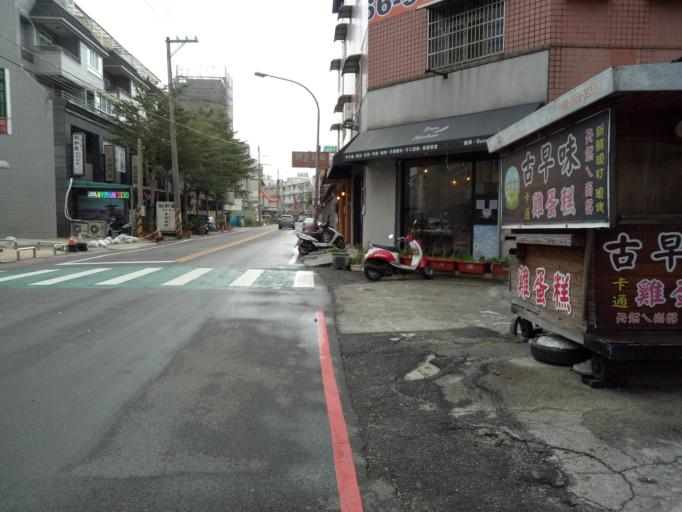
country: TW
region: Taiwan
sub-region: Taoyuan
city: Taoyuan
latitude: 24.9670
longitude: 121.3034
